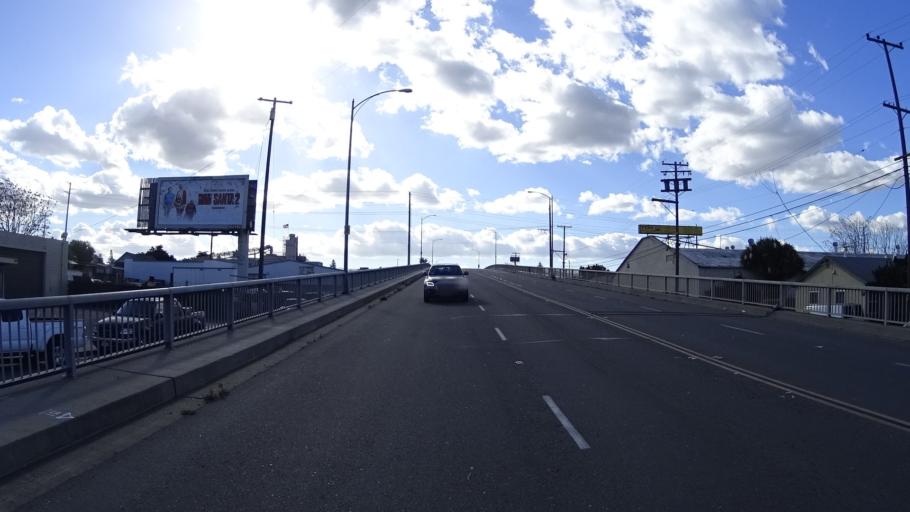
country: US
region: California
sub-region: Santa Clara County
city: San Jose
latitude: 37.3452
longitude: -121.9165
